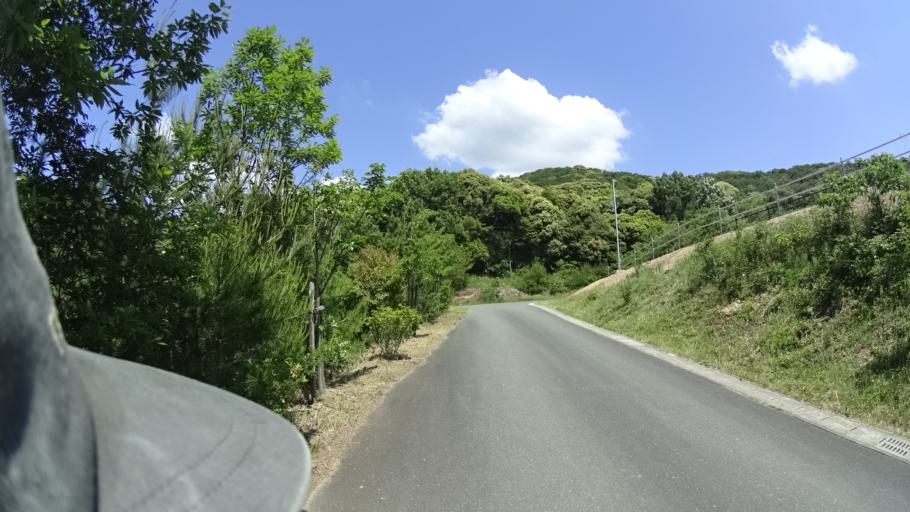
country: JP
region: Shizuoka
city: Kosai-shi
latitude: 34.7364
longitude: 137.4824
